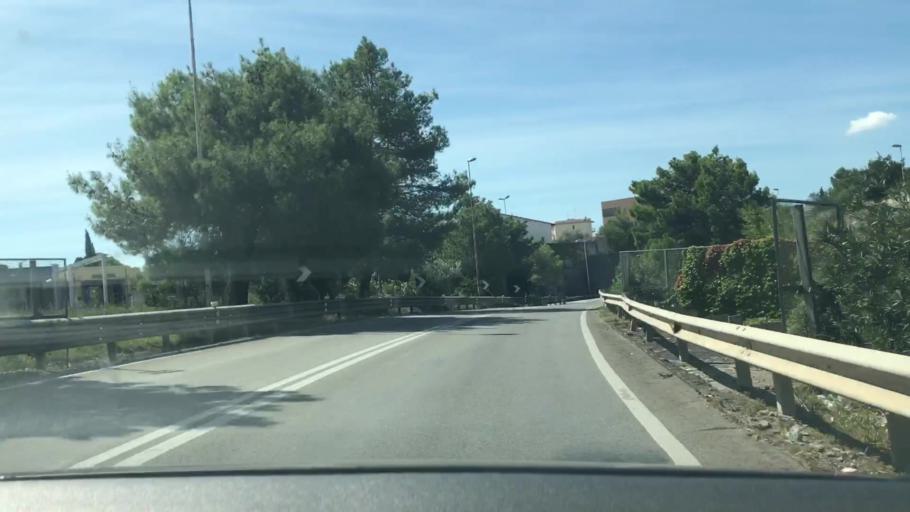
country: IT
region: Basilicate
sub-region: Provincia di Matera
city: Matera
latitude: 40.6824
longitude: 16.5898
